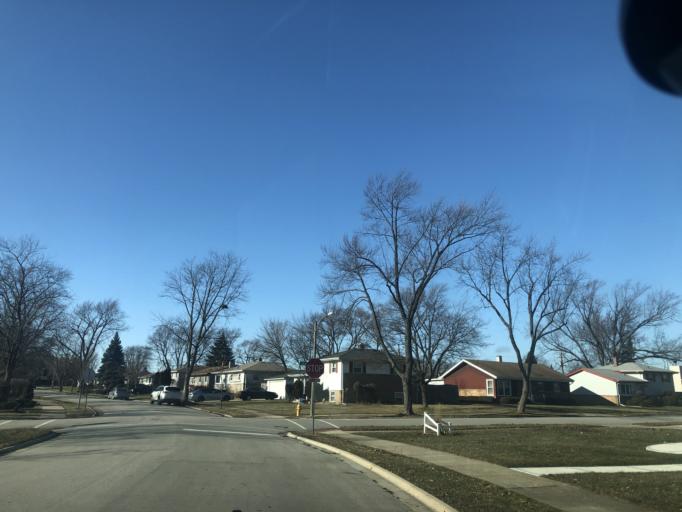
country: US
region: Illinois
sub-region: DuPage County
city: Addison
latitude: 41.9293
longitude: -87.9999
